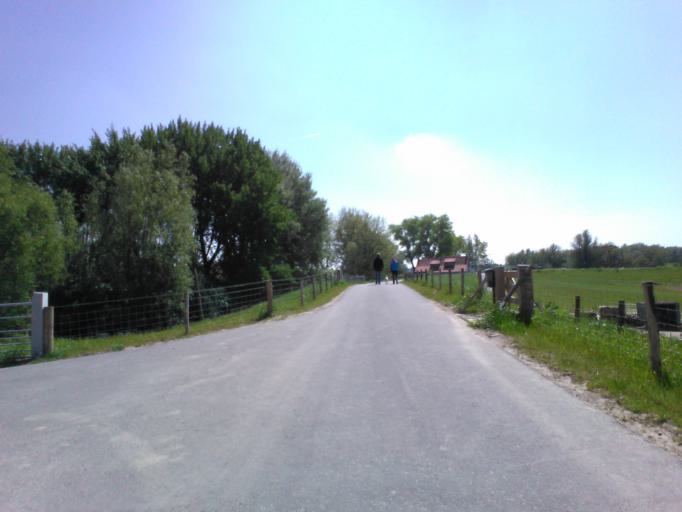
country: NL
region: South Holland
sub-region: Gemeente Sliedrecht
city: Sliedrecht
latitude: 51.7900
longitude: 4.7575
